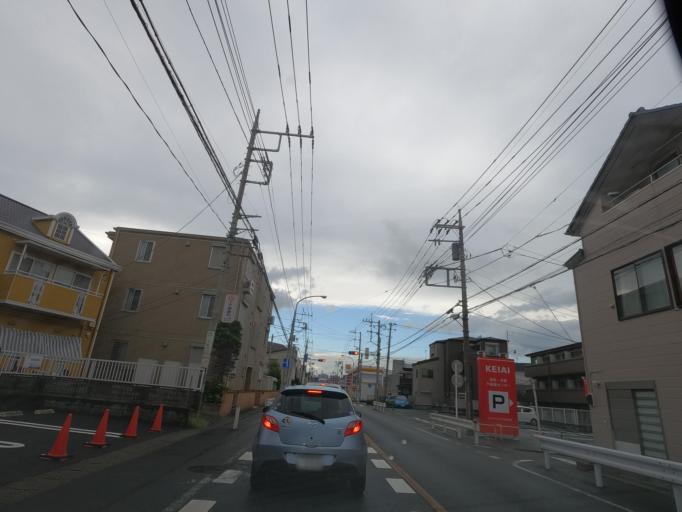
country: JP
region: Saitama
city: Yono
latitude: 35.8845
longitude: 139.6488
